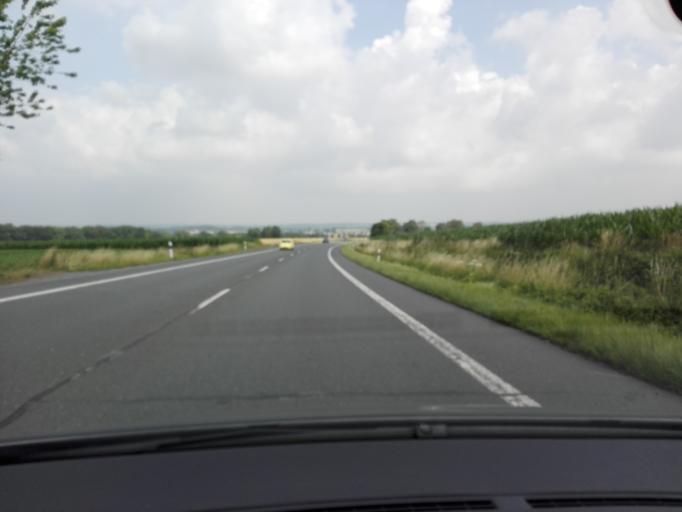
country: DE
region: North Rhine-Westphalia
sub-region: Regierungsbezirk Arnsberg
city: Frondenberg
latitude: 51.5332
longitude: 7.7699
